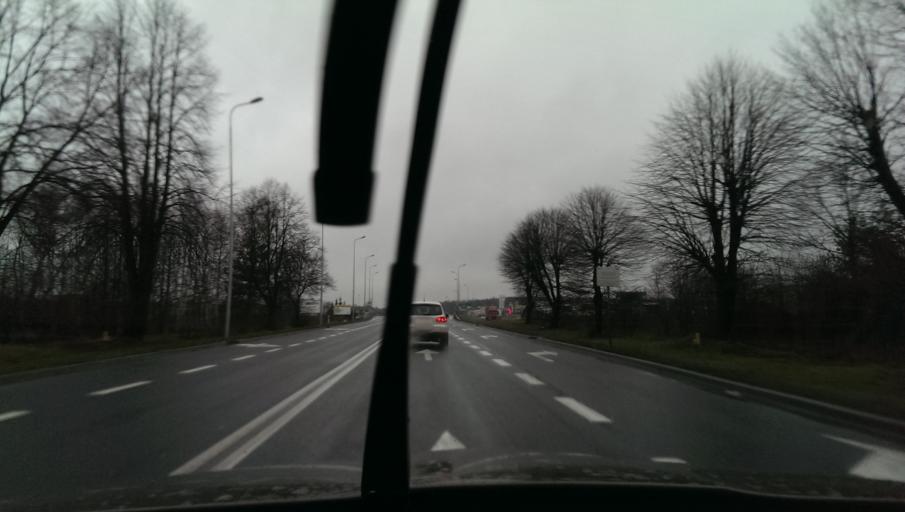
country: PL
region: Subcarpathian Voivodeship
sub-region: Powiat rzeszowski
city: Rudna Mala
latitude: 50.1117
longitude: 21.9741
